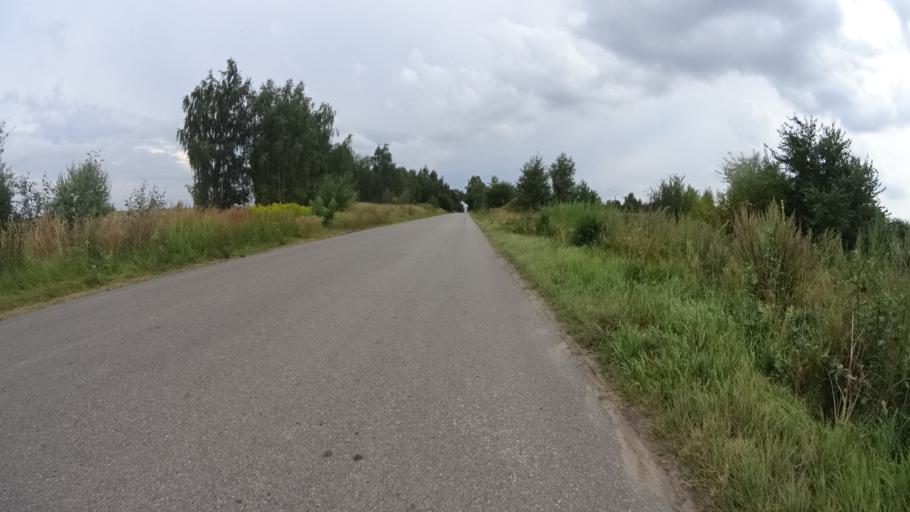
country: PL
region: Masovian Voivodeship
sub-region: Powiat grojecki
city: Goszczyn
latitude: 51.6713
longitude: 20.8573
